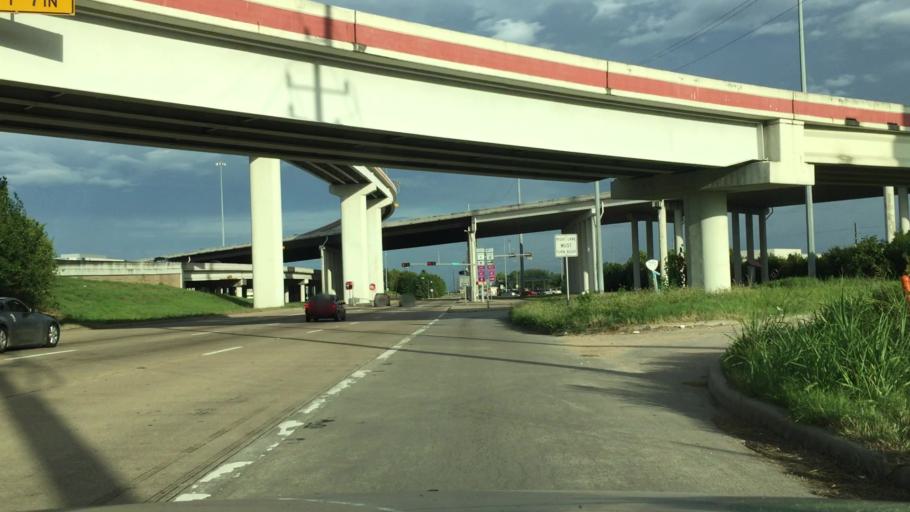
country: US
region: Texas
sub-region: Harris County
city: Hudson
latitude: 29.9381
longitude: -95.5187
